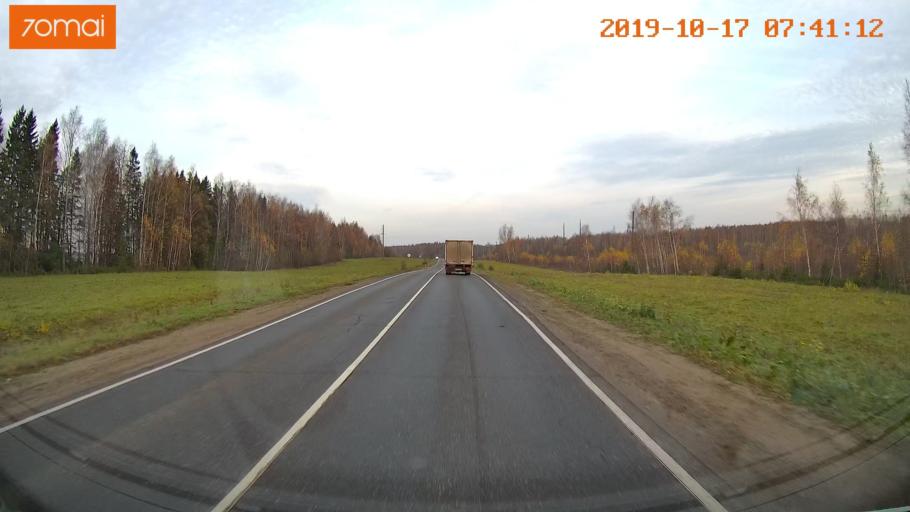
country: RU
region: Vladimir
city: Yur'yev-Pol'skiy
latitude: 56.4803
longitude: 39.8150
